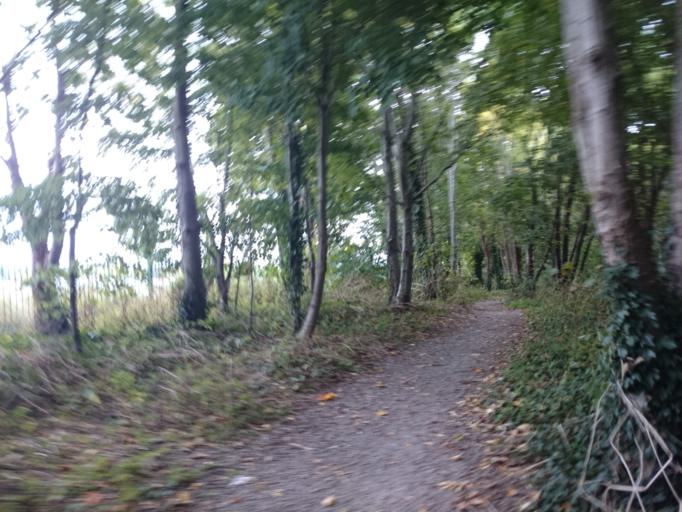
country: IE
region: Leinster
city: Shankill
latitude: 53.2252
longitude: -6.1136
